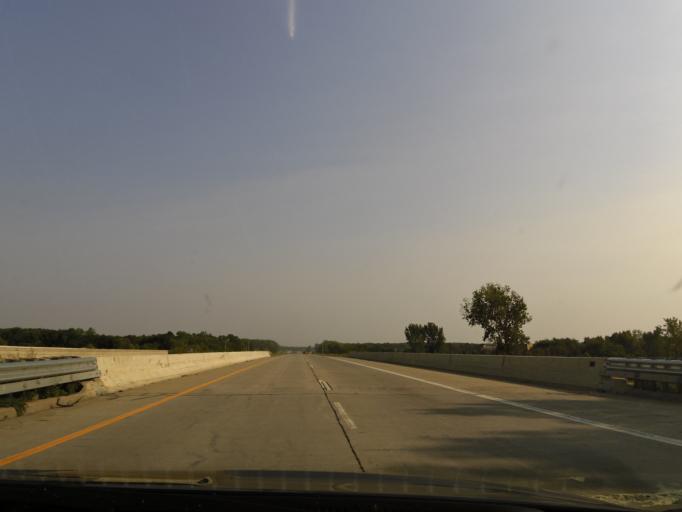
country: US
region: Minnesota
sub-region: Stearns County
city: Saint Joseph
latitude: 45.5587
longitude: -94.3406
